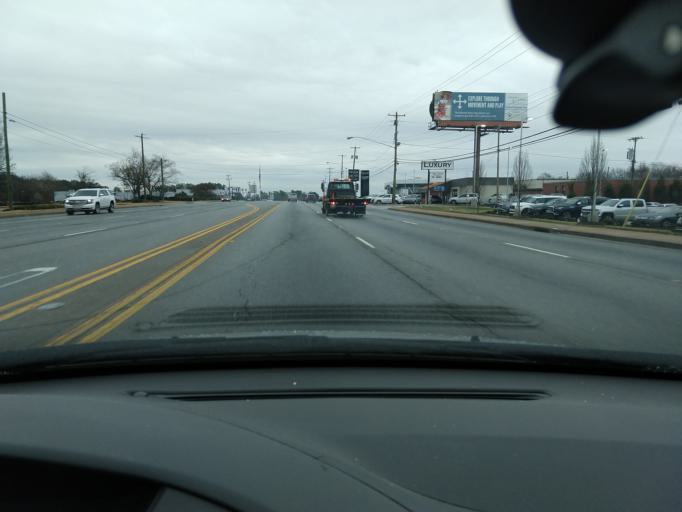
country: US
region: South Carolina
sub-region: Greenville County
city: Greenville
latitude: 34.8246
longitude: -82.3443
